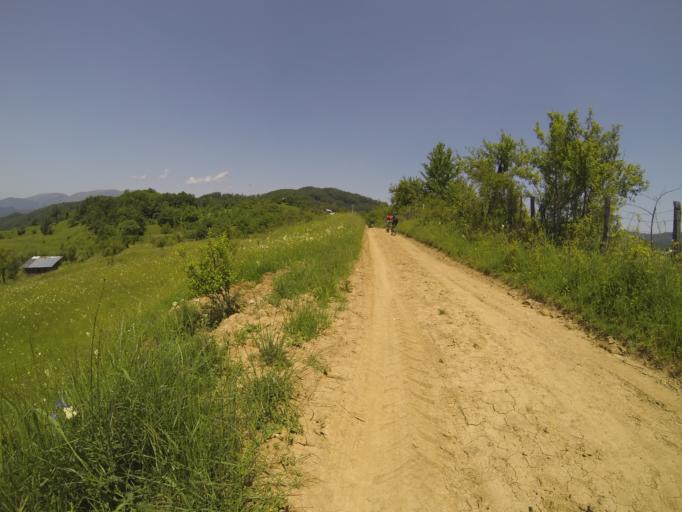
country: RO
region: Valcea
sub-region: Oras Baile Olanesti
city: Cheia
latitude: 45.2032
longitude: 24.2127
